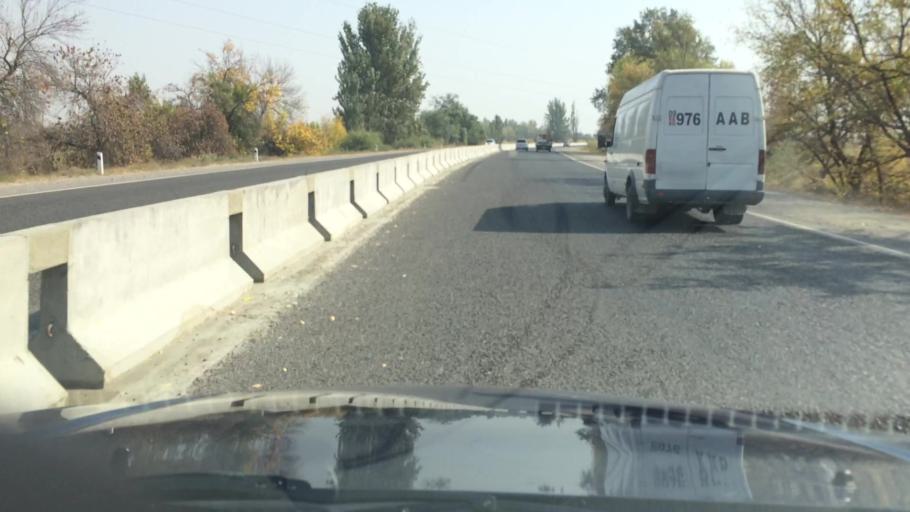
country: KG
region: Chuy
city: Kant
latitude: 42.9763
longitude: 74.8862
